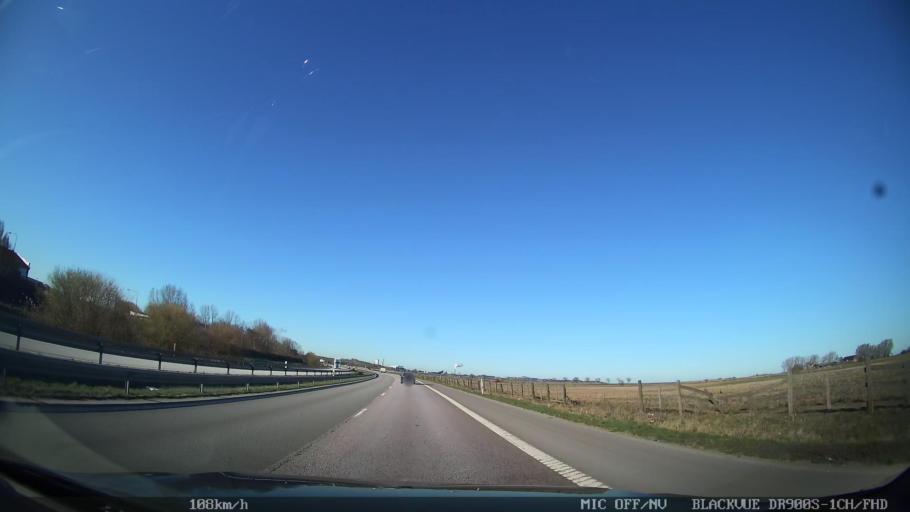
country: SE
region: Skane
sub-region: Burlovs Kommun
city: Arloev
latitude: 55.6451
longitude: 13.0656
